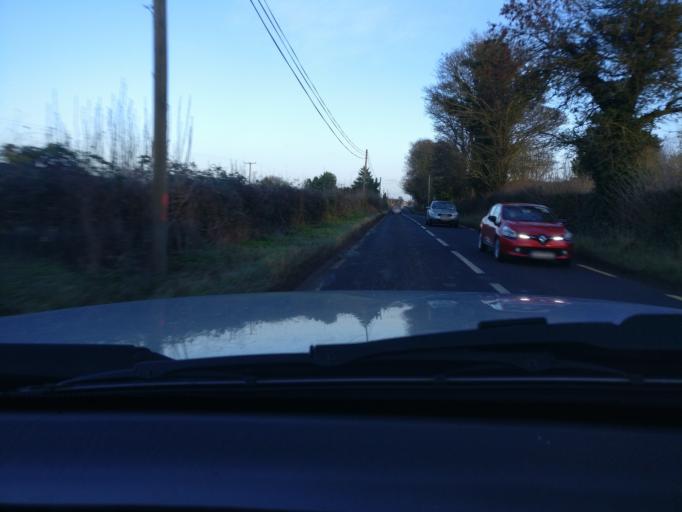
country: IE
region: Leinster
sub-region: Lu
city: Ardee
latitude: 53.8527
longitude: -6.5770
